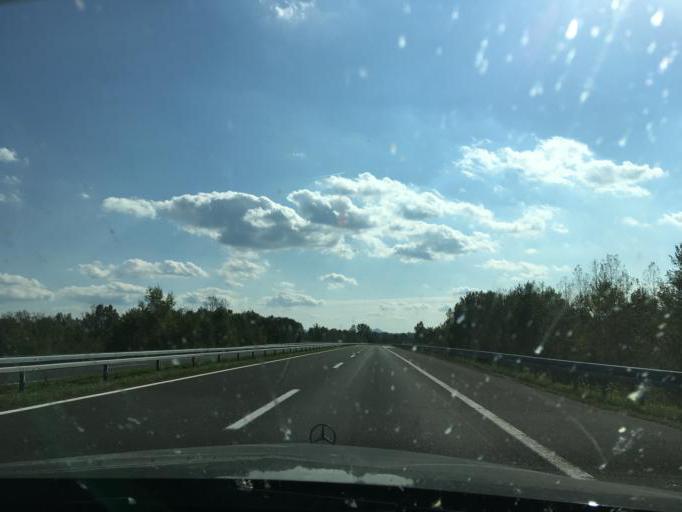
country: HR
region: Medimurska
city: Orehovica
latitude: 46.3077
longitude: 16.5055
